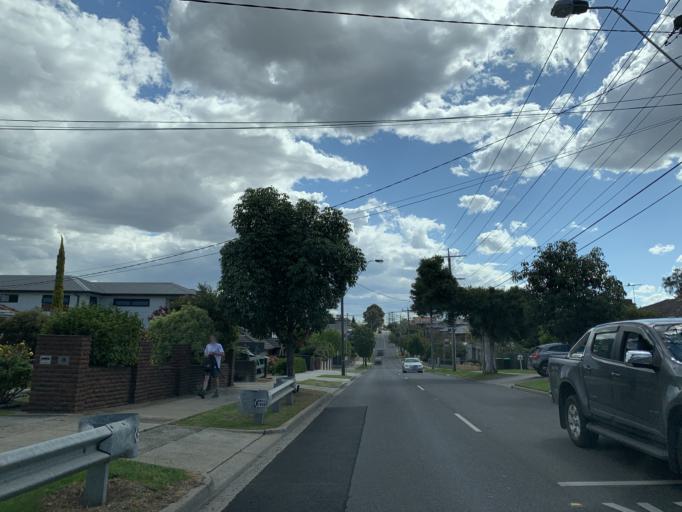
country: AU
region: Victoria
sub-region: Moonee Valley
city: Niddrie
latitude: -37.7489
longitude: 144.8902
